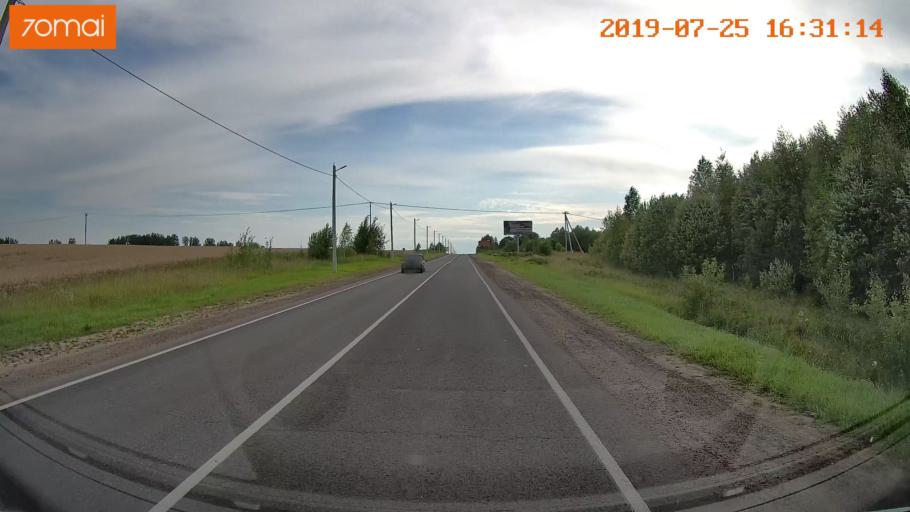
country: RU
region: Ivanovo
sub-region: Privolzhskiy Rayon
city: Ples
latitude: 57.4442
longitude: 41.4883
